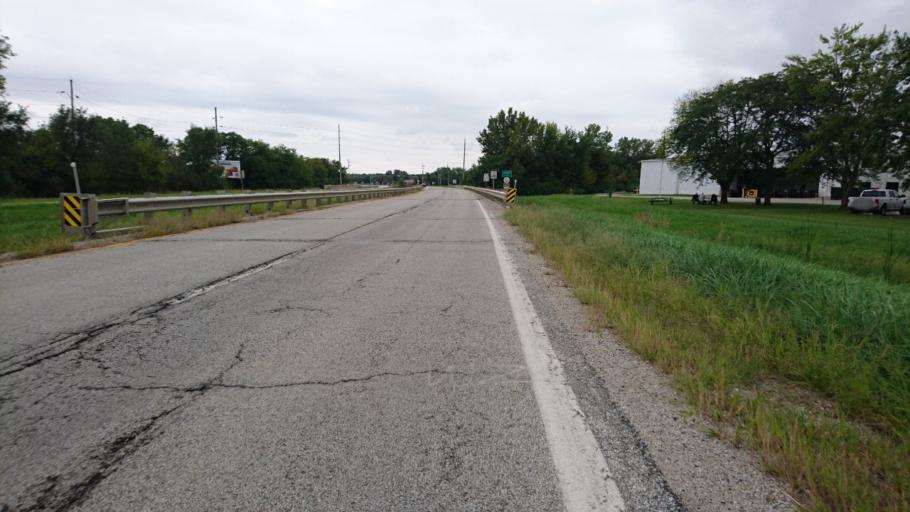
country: US
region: Illinois
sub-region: Livingston County
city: Pontiac
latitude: 40.8895
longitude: -88.6397
